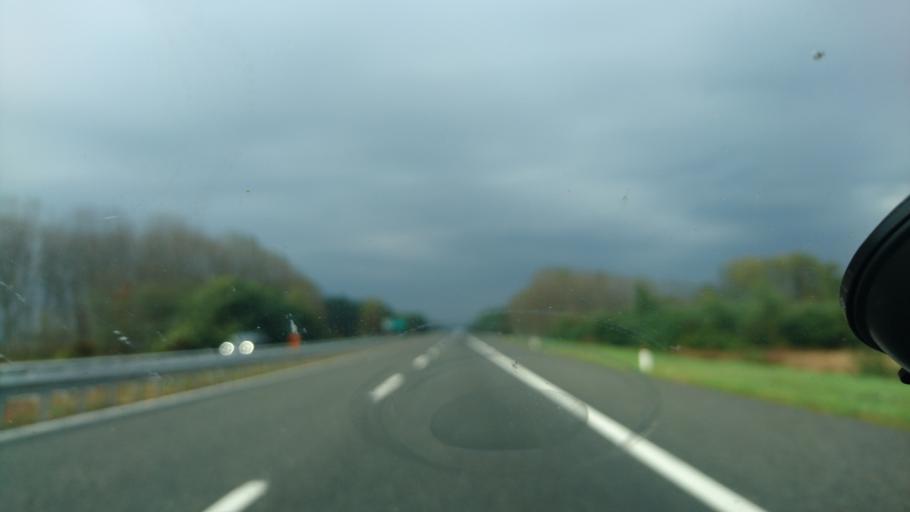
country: IT
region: Piedmont
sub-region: Provincia di Novara
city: Carpignano Sesia
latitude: 45.5471
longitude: 8.4247
